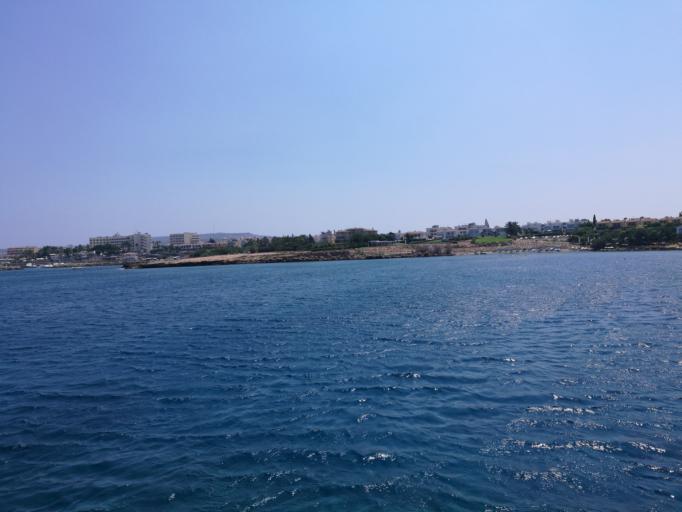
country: CY
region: Ammochostos
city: Protaras
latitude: 35.0430
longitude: 34.0367
